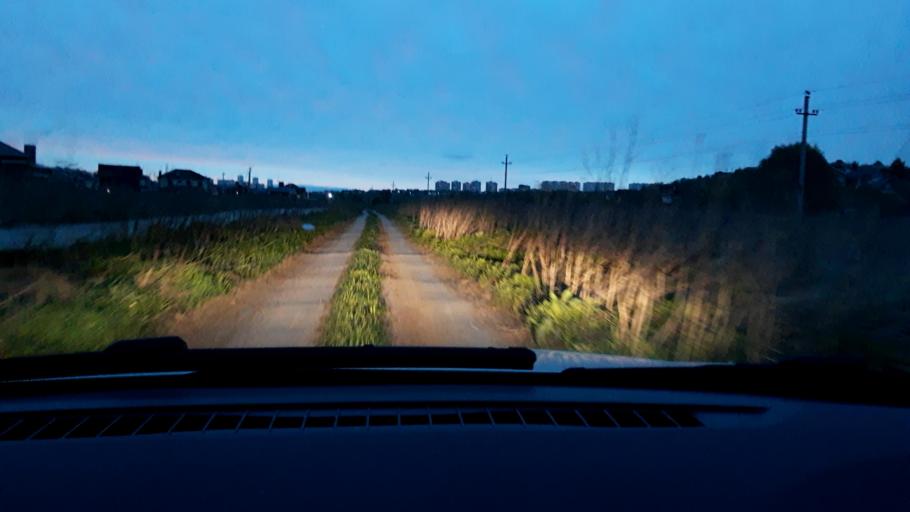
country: RU
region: Nizjnij Novgorod
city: Afonino
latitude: 56.2620
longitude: 44.0796
